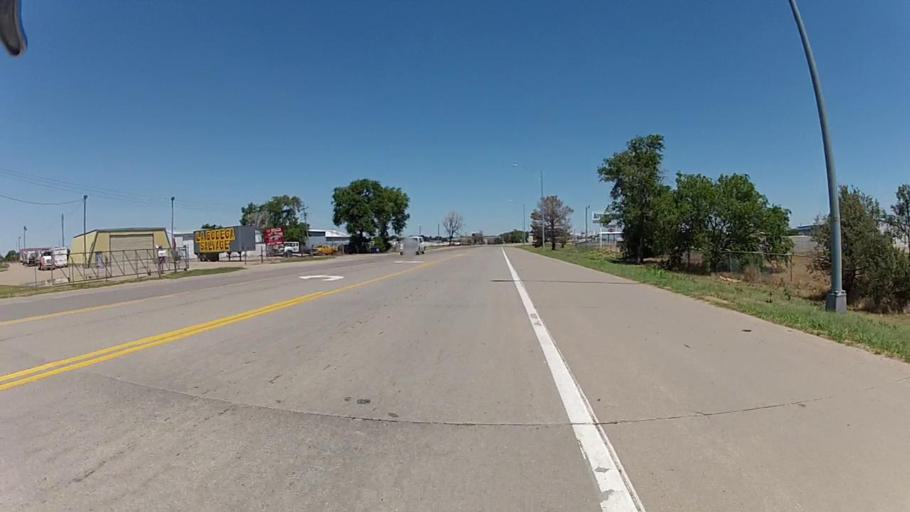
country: US
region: Kansas
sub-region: Ford County
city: Dodge City
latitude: 37.7279
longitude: -100.0177
